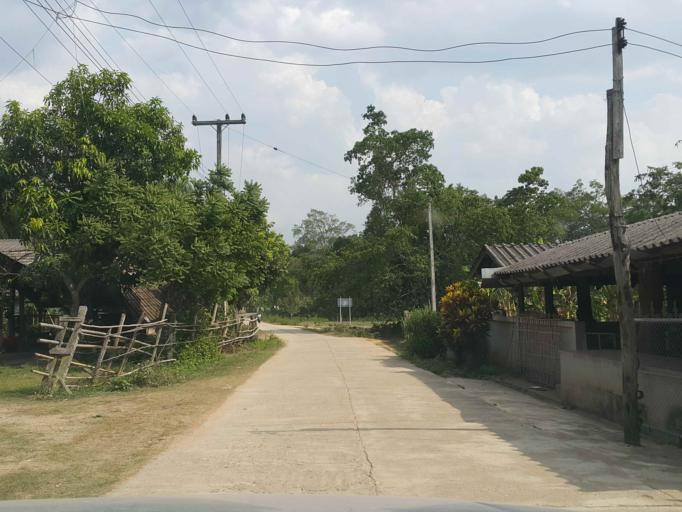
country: TH
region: Chiang Mai
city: Wiang Haeng
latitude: 19.3932
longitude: 98.7219
